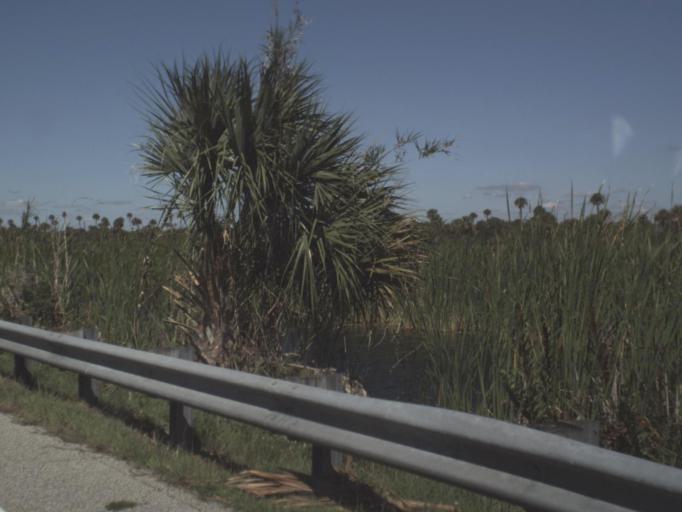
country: US
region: Florida
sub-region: Collier County
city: Marco
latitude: 25.9293
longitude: -81.4355
